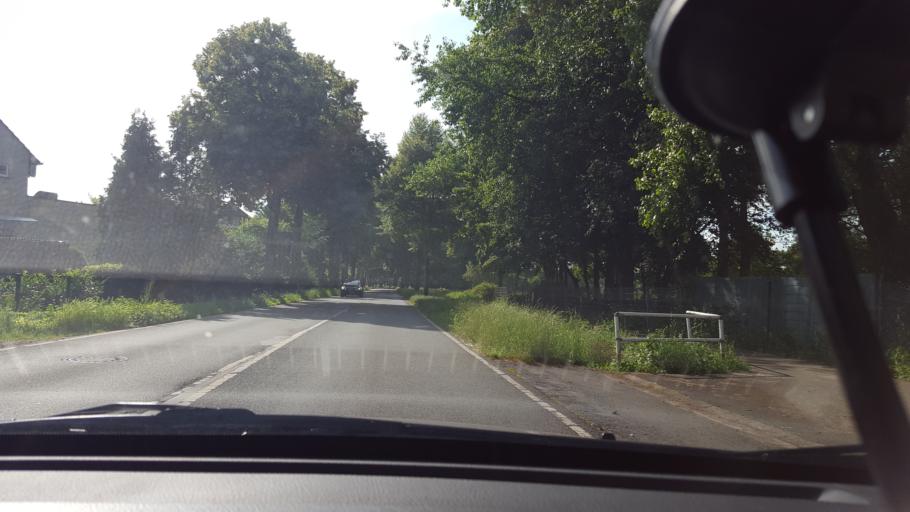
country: DE
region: North Rhine-Westphalia
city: Marl
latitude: 51.6568
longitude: 7.0667
